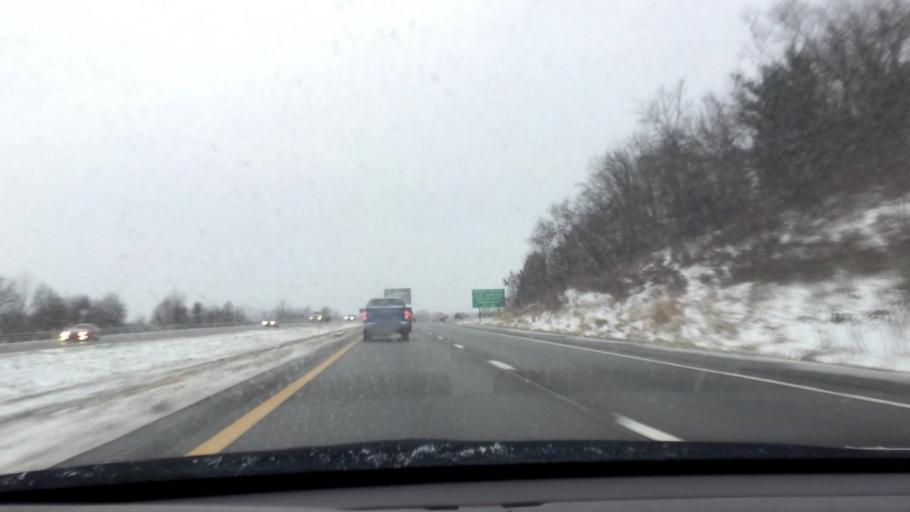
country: US
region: Pennsylvania
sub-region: Washington County
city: Canonsburg
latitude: 40.2859
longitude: -80.1670
